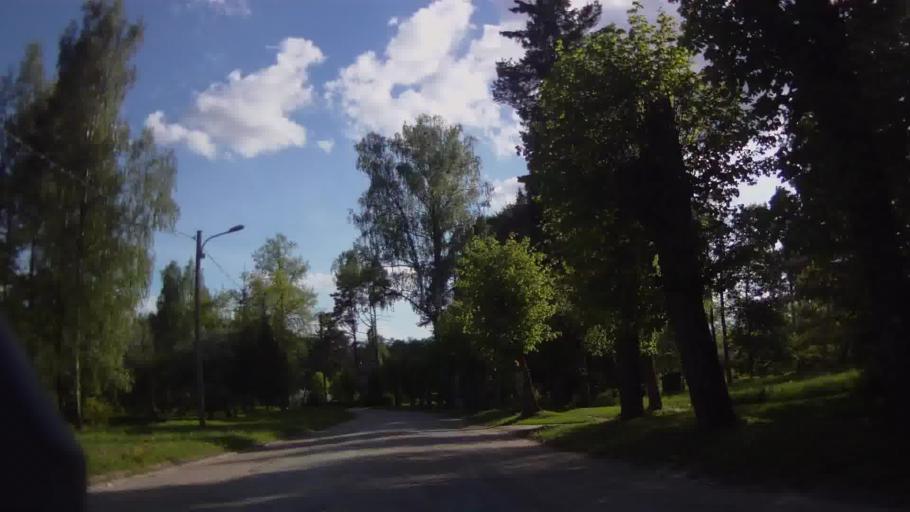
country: LV
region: Baldone
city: Baldone
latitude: 56.7447
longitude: 24.4070
